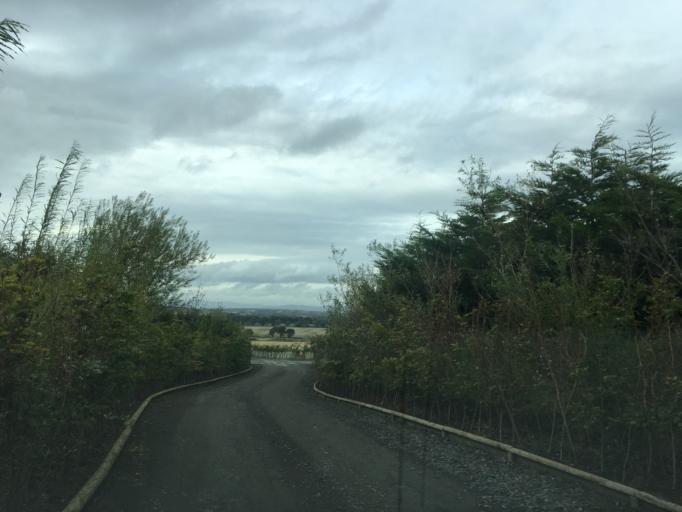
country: GB
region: Scotland
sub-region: West Lothian
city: Kirknewton
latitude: 55.9076
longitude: -3.4188
